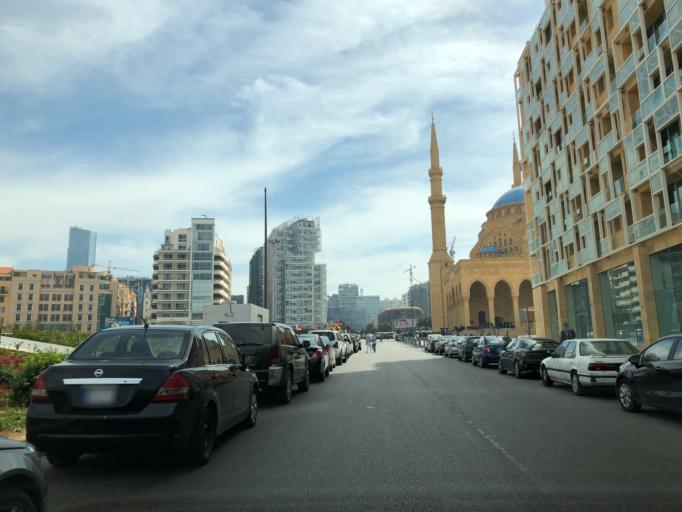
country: LB
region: Beyrouth
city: Beirut
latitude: 33.8966
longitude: 35.5069
